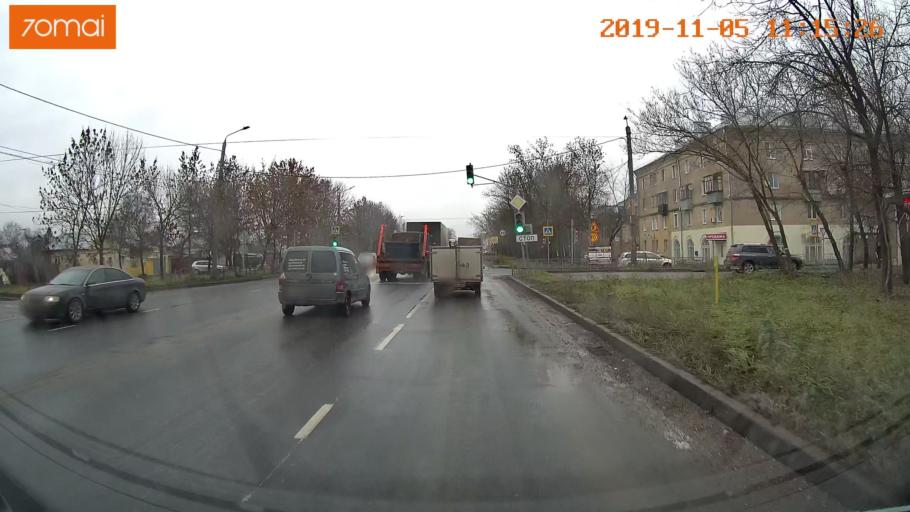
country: RU
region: Ivanovo
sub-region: Gorod Ivanovo
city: Ivanovo
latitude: 56.9777
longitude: 40.9542
